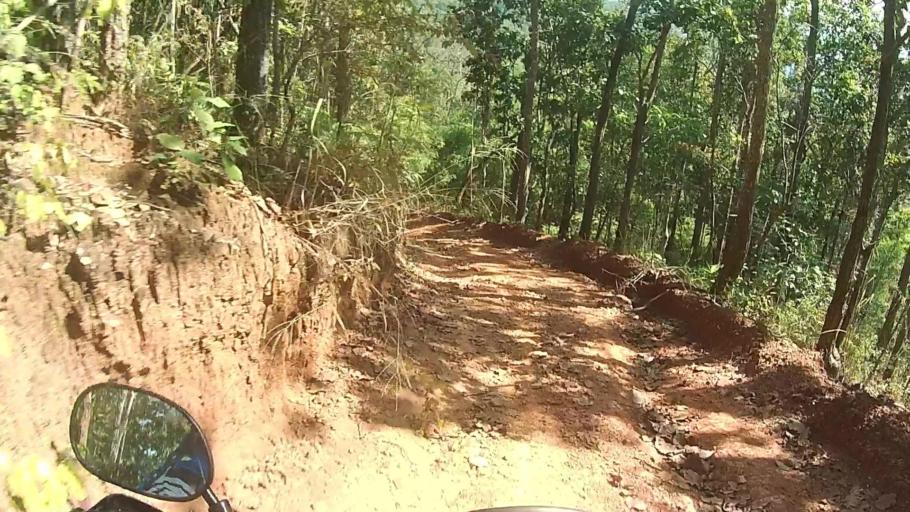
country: TH
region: Chiang Mai
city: Mae On
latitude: 19.0283
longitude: 99.2964
